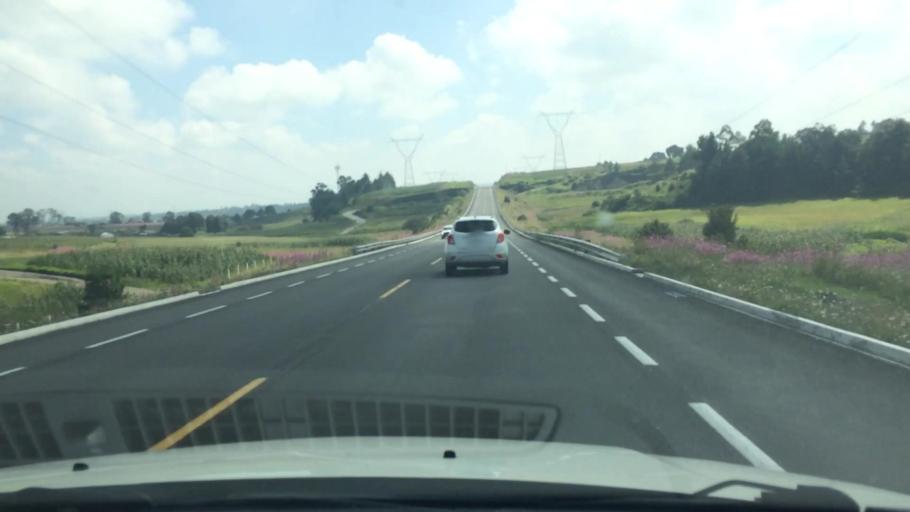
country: MX
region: Mexico
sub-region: Almoloya de Juarez
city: San Pedro de la Hortaliza (Ejido Almoloyan)
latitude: 19.3783
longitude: -99.8386
